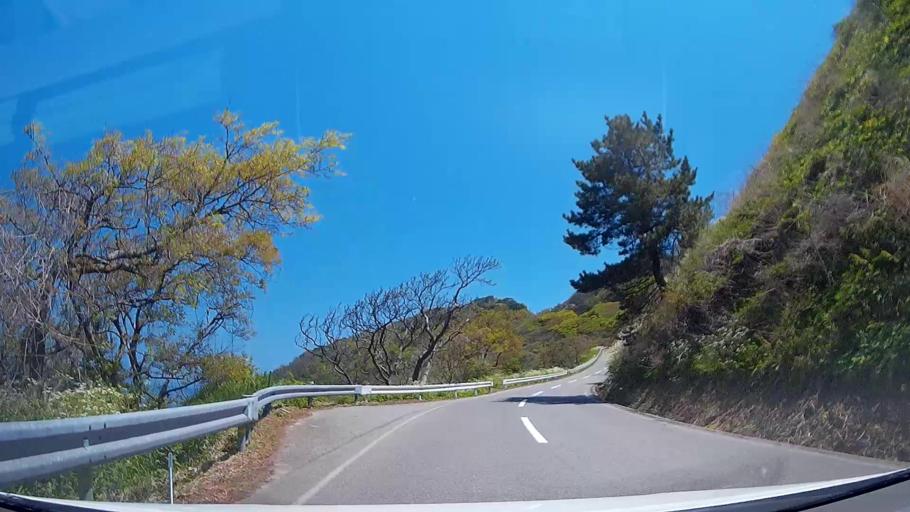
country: JP
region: Ishikawa
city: Nanao
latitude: 37.5246
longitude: 137.2528
